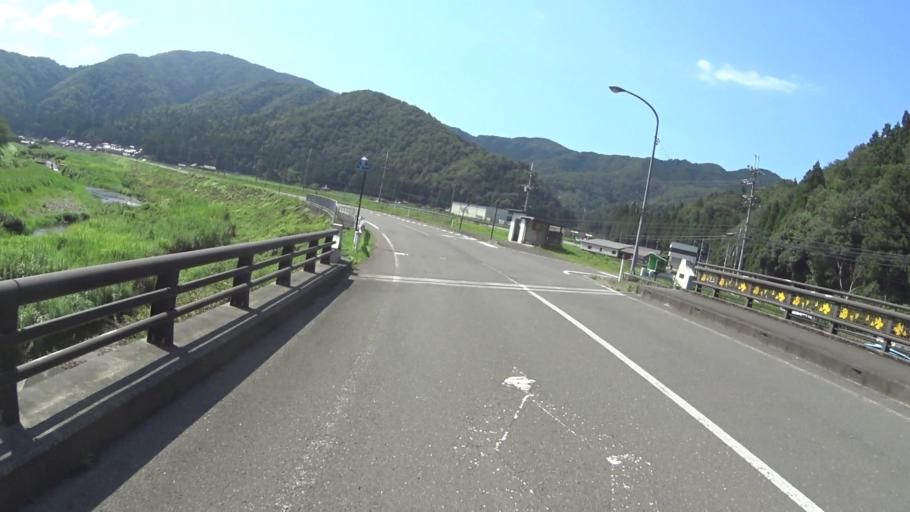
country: JP
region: Fukui
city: Obama
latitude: 35.4087
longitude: 135.6406
